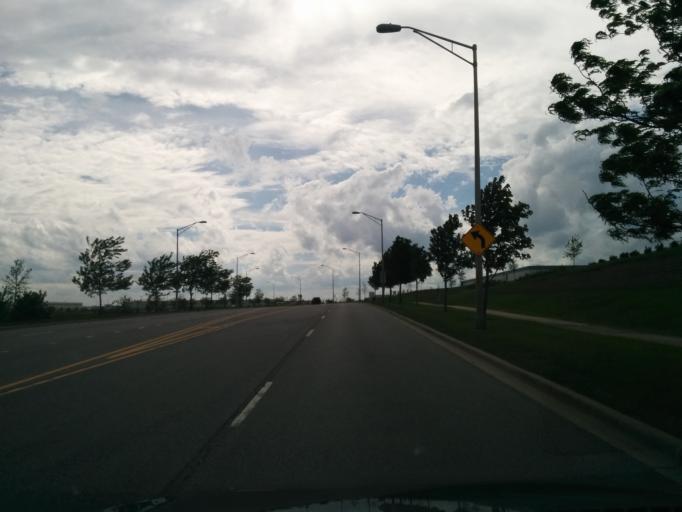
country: US
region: Illinois
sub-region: Will County
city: Romeoville
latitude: 41.6249
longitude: -88.0986
